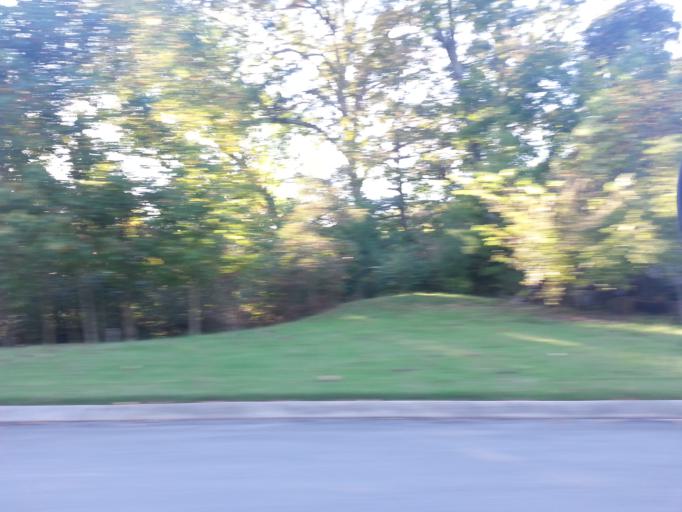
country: US
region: Tennessee
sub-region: Blount County
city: Eagleton Village
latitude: 35.7866
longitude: -83.9316
